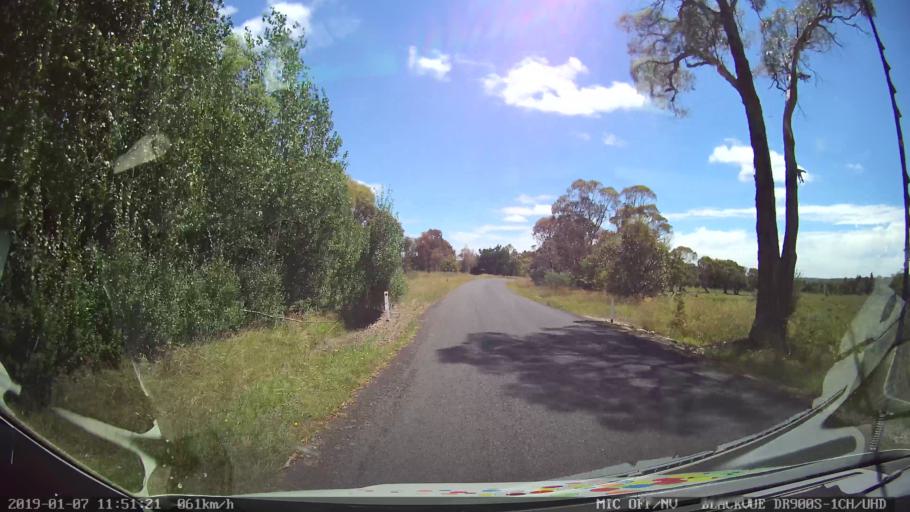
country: AU
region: New South Wales
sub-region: Guyra
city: Guyra
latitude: -30.3089
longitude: 151.6451
